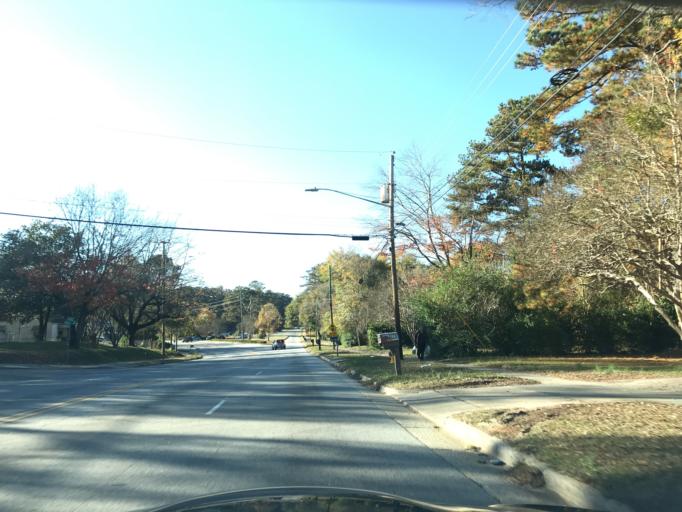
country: US
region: North Carolina
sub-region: Wake County
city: Raleigh
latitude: 35.7723
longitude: -78.5976
